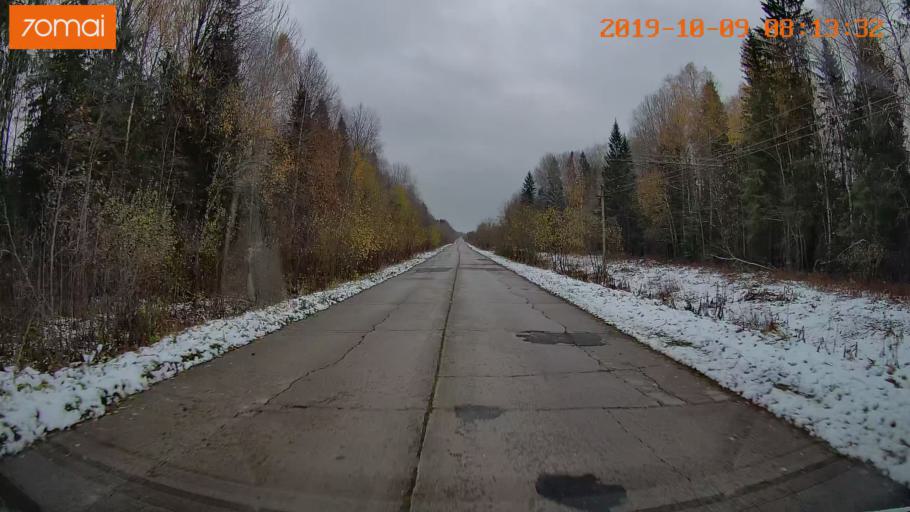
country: RU
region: Vologda
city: Gryazovets
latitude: 58.7240
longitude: 40.1417
